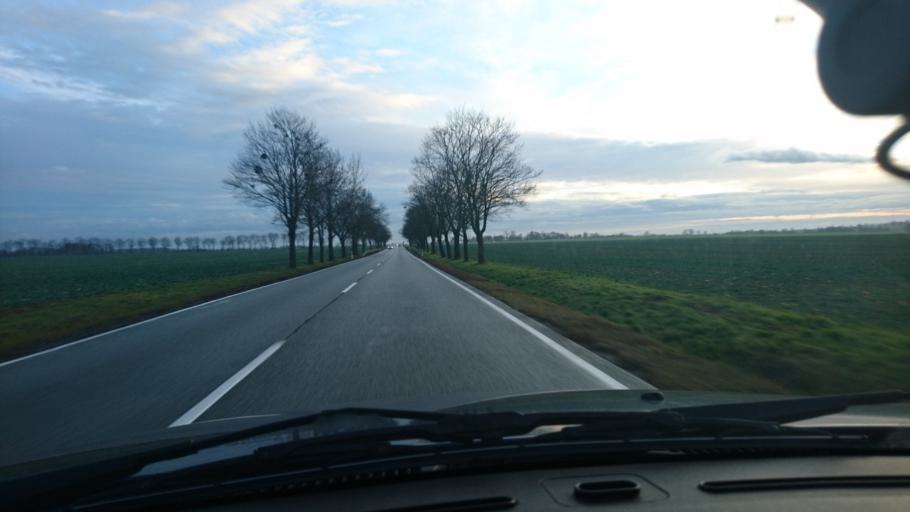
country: PL
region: Opole Voivodeship
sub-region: Powiat kluczborski
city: Byczyna
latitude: 51.0757
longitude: 18.2014
